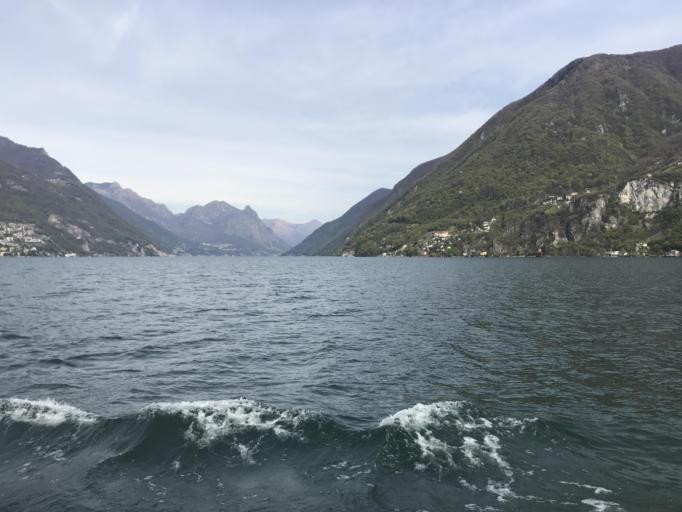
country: IT
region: Lombardy
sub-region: Provincia di Como
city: Campione
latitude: 45.9806
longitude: 8.9608
